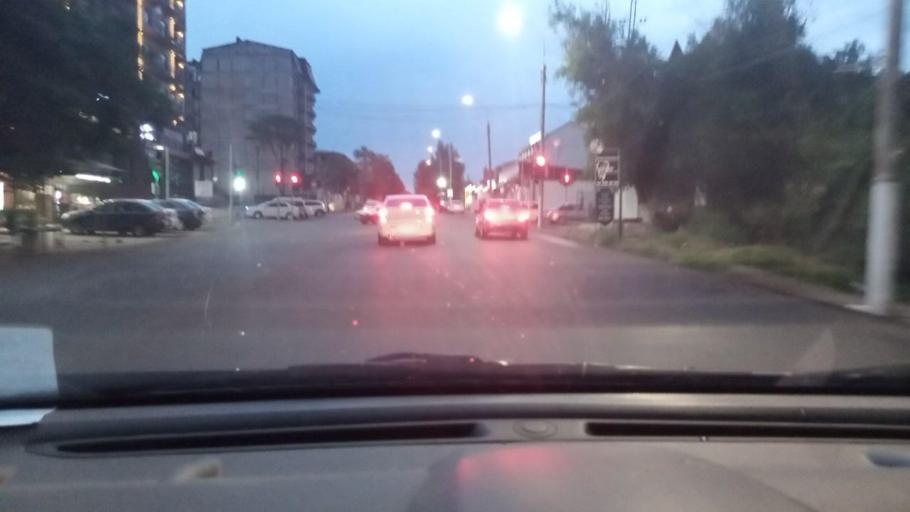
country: UZ
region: Toshkent
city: Salor
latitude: 41.3174
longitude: 69.3388
